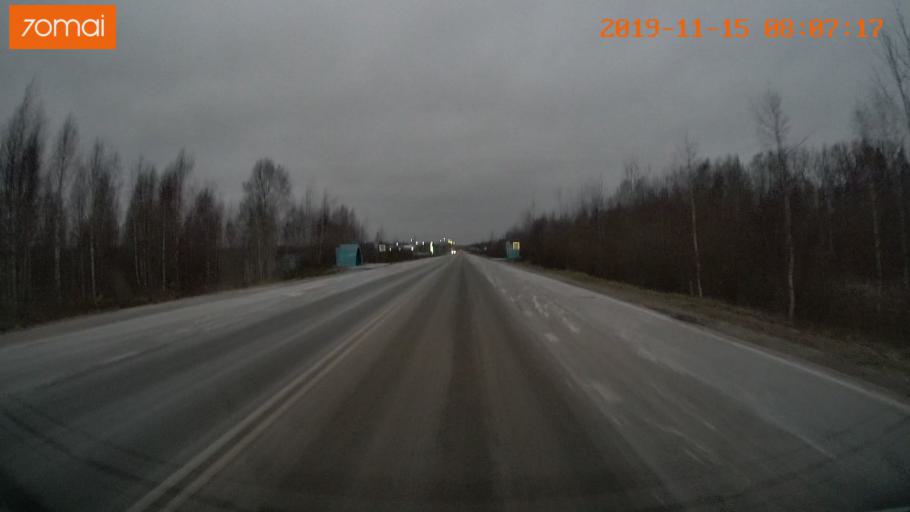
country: RU
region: Vologda
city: Cherepovets
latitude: 59.0257
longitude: 38.0208
